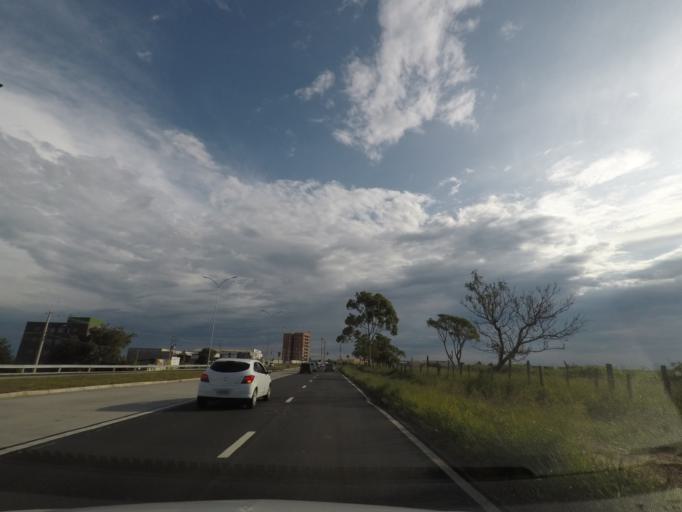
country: BR
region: Sao Paulo
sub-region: Campinas
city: Campinas
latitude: -22.9391
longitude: -47.1422
